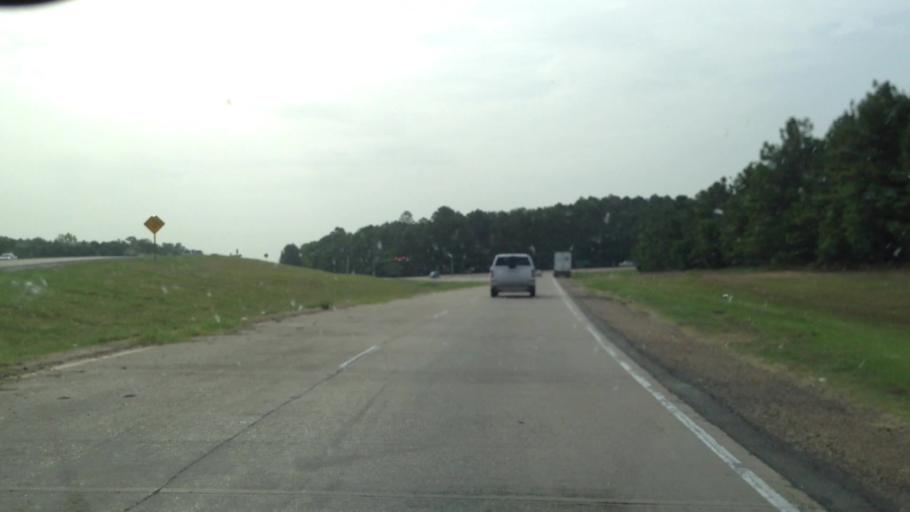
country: US
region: Louisiana
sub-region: Caddo Parish
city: Shreveport
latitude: 32.4170
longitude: -93.8177
